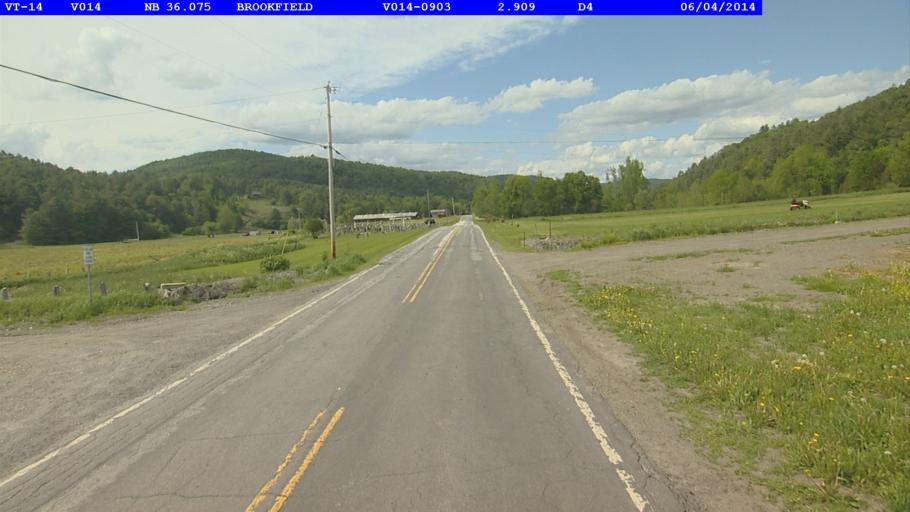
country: US
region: Vermont
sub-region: Orange County
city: Williamstown
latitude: 44.0189
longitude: -72.5703
